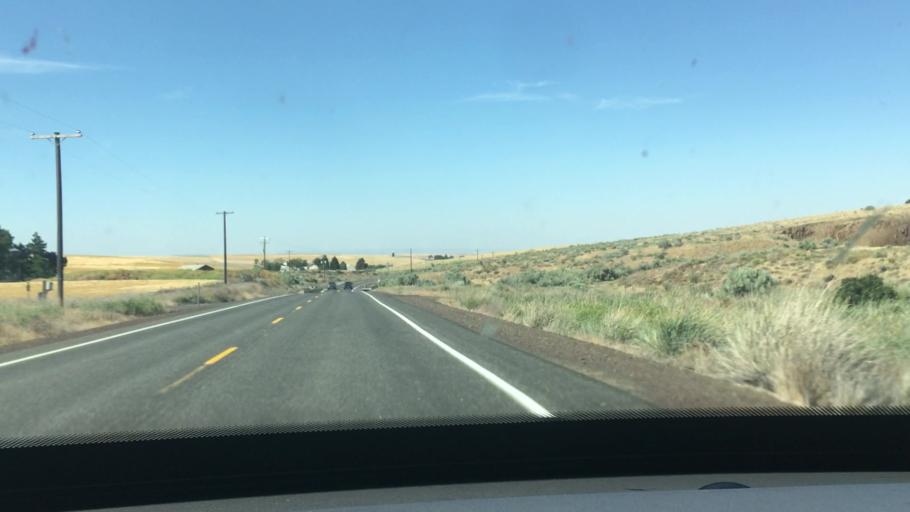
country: US
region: Oregon
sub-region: Sherman County
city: Moro
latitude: 45.4511
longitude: -120.7522
